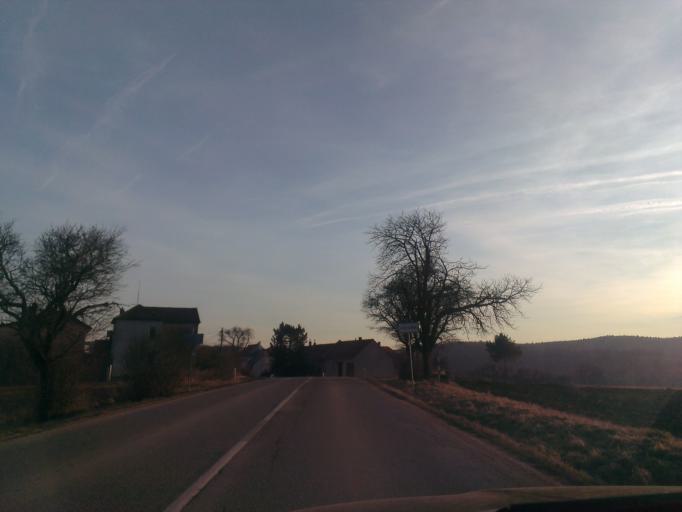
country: CZ
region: South Moravian
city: Bilovice nad Svitavou
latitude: 49.2606
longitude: 16.7299
